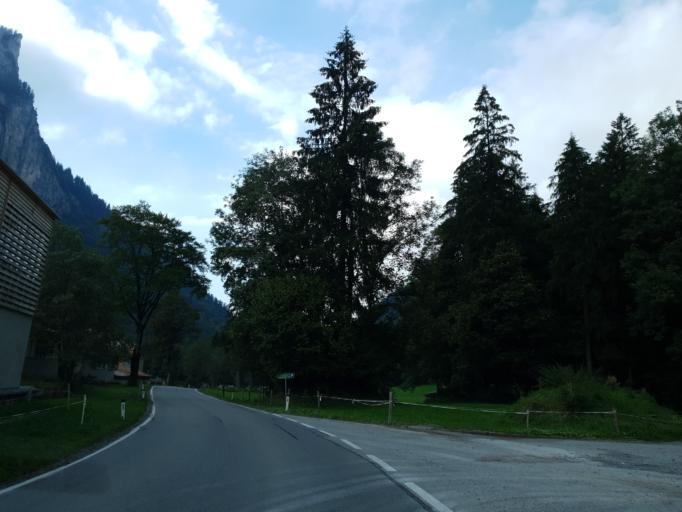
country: AT
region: Vorarlberg
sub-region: Politischer Bezirk Bregenz
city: Au
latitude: 47.3307
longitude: 9.9716
